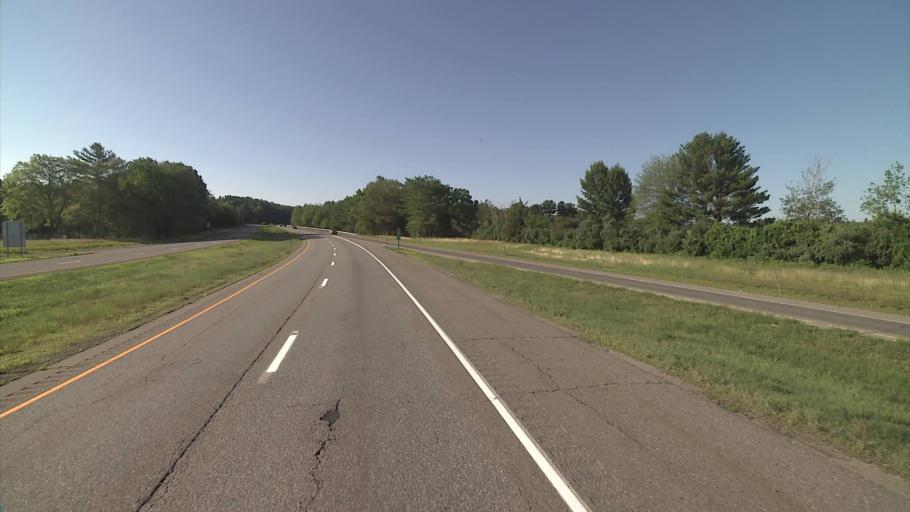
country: US
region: Connecticut
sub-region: Windham County
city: Killingly Center
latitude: 41.8409
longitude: -71.8788
